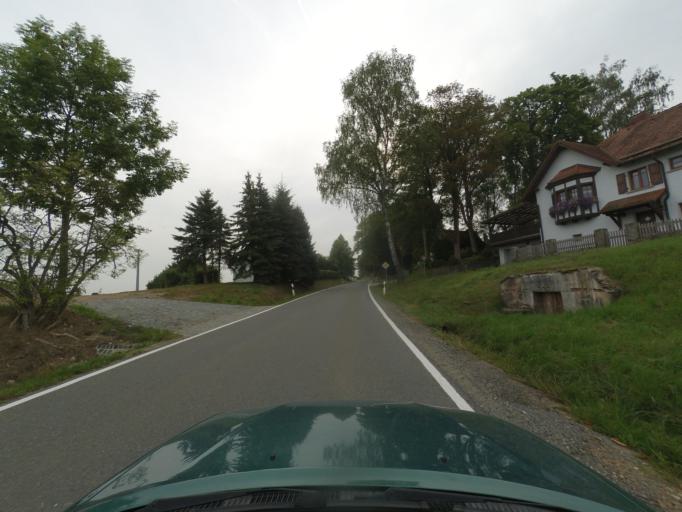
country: DE
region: Bavaria
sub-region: Upper Palatinate
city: Eslarn
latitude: 49.5803
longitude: 12.5277
